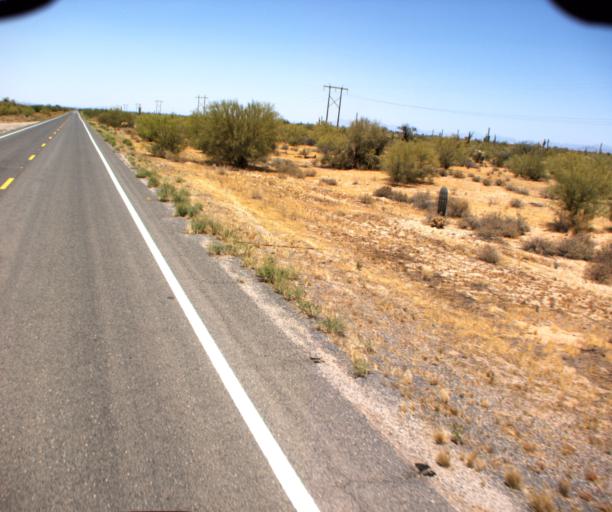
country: US
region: Arizona
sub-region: Pinal County
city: Florence
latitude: 32.8985
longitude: -111.2765
